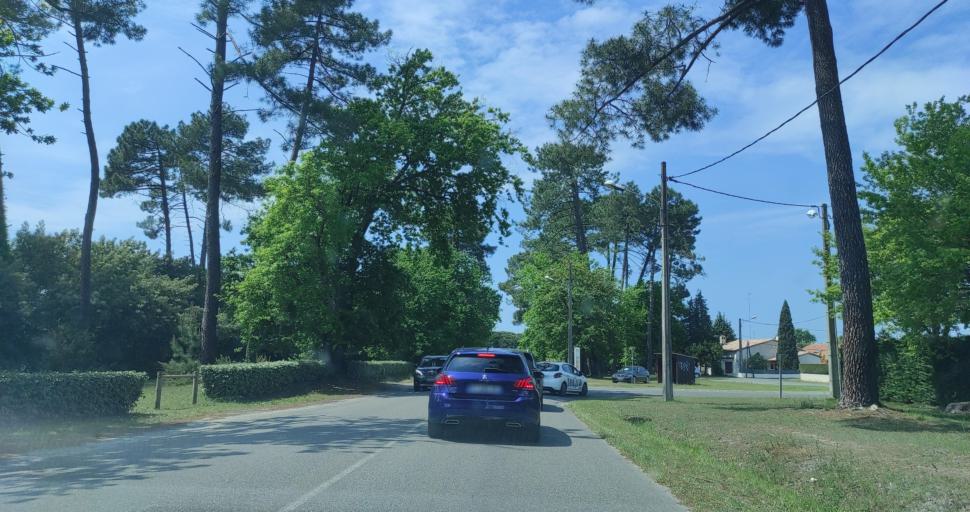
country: FR
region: Aquitaine
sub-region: Departement de la Gironde
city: Ares
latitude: 44.7605
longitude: -1.1260
